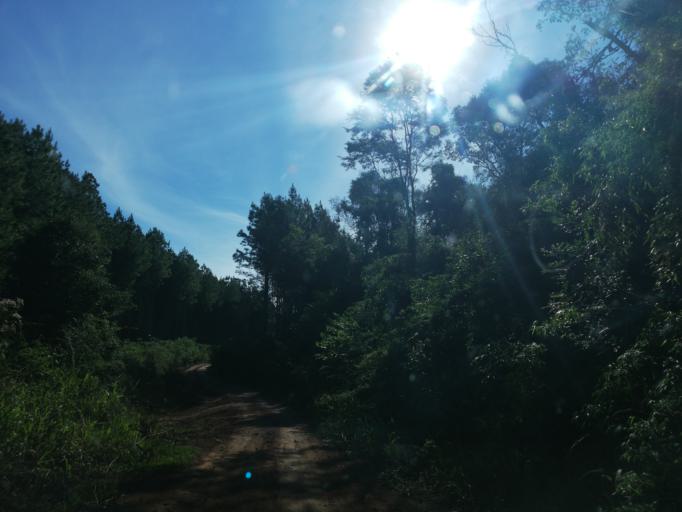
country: AR
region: Misiones
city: Dos de Mayo
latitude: -27.0158
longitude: -54.4400
